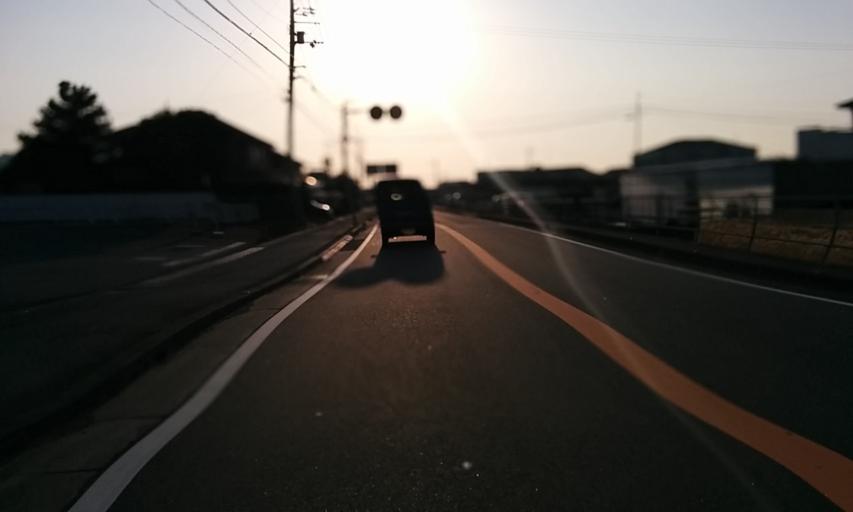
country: JP
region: Ehime
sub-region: Shikoku-chuo Shi
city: Matsuyama
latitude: 33.7825
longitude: 132.8051
